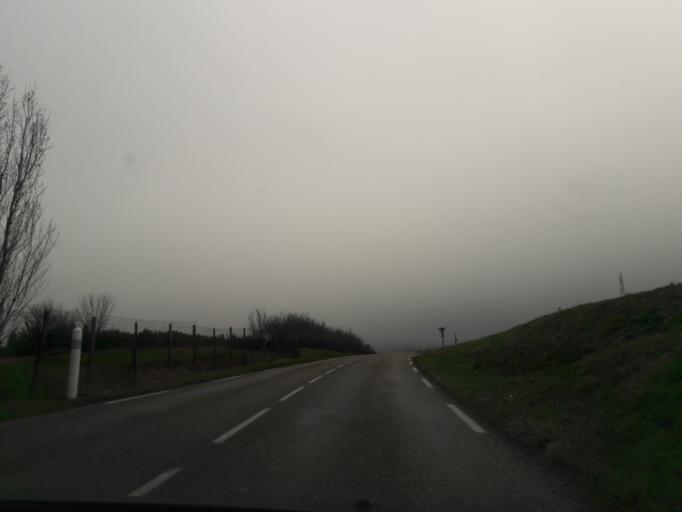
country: FR
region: Rhone-Alpes
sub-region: Departement de l'Isere
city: Gillonnay
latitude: 45.3787
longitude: 5.2815
